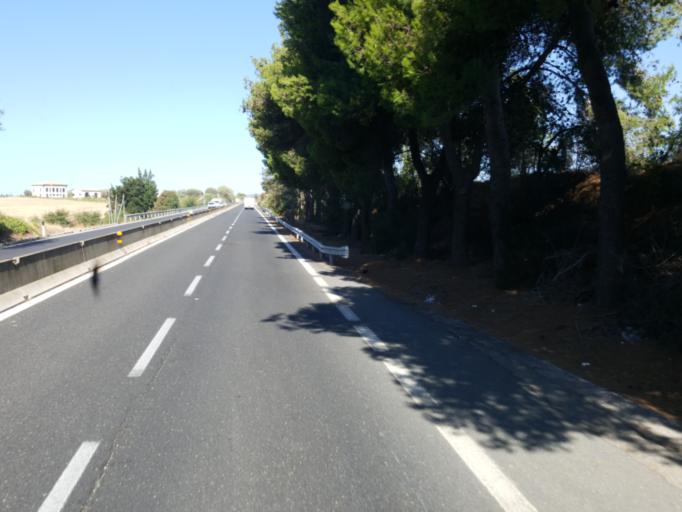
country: IT
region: Latium
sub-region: Provincia di Viterbo
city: Pescia Romana
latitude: 42.4057
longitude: 11.4881
